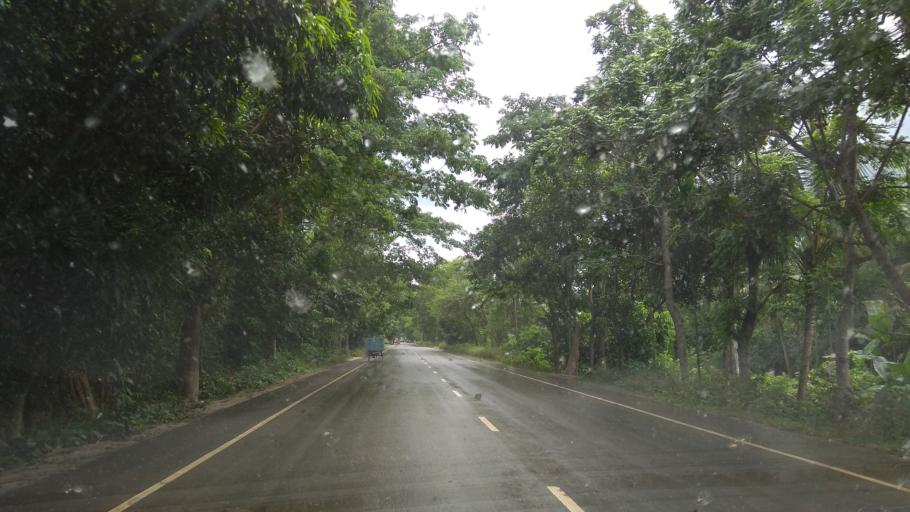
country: BD
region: Khulna
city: Kalia
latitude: 23.2470
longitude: 89.7561
